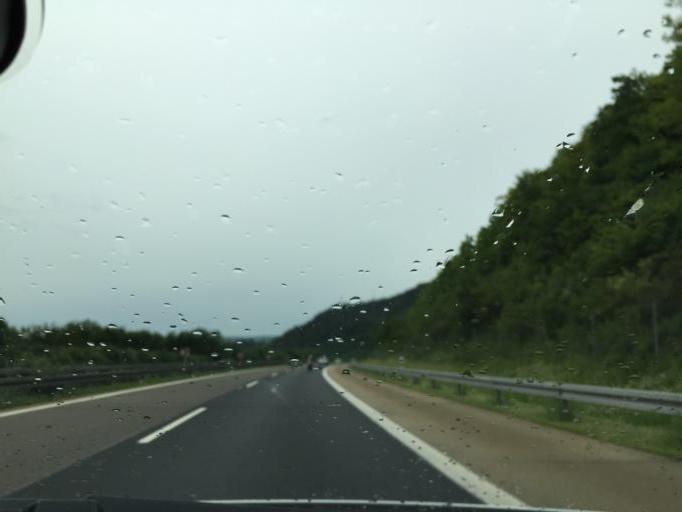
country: DE
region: Bavaria
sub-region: Regierungsbezirk Unterfranken
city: Elfershausen
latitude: 50.1504
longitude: 9.9584
